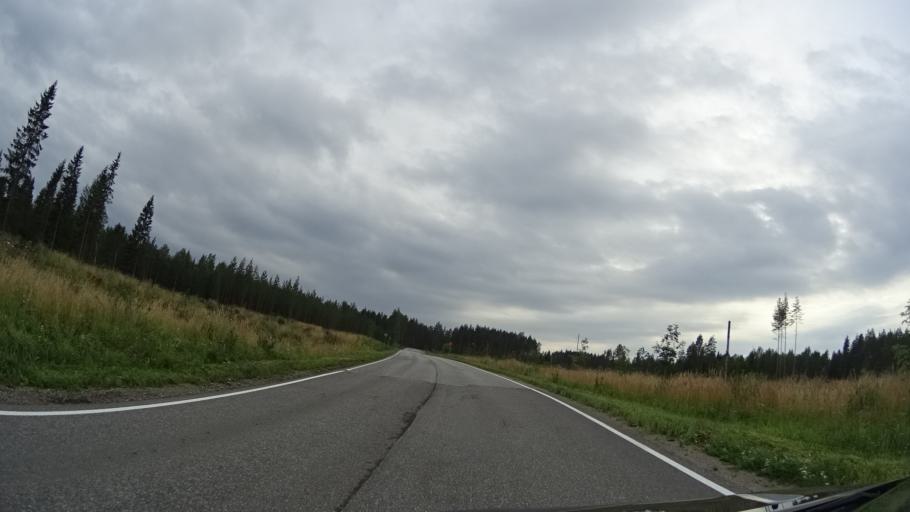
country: FI
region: Southern Savonia
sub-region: Savonlinna
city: Punkaharju
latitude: 61.7549
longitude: 29.4508
